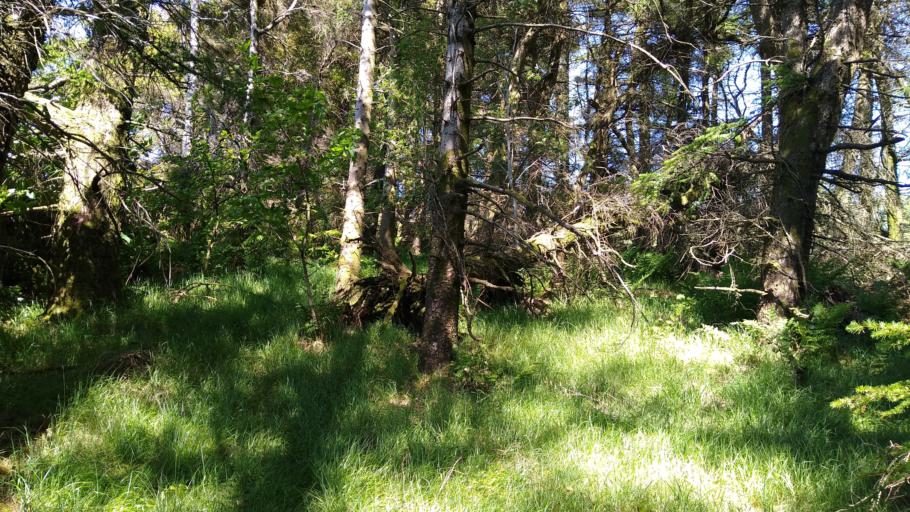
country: GB
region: England
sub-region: Cumbria
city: Wigton
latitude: 54.7523
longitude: -3.0819
